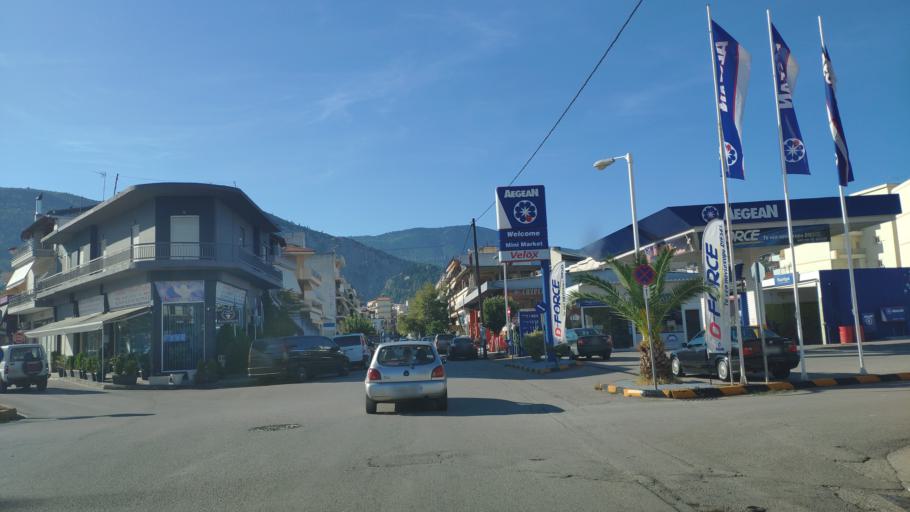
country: GR
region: Central Greece
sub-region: Nomos Voiotias
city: Livadeia
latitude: 38.4431
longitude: 22.8787
